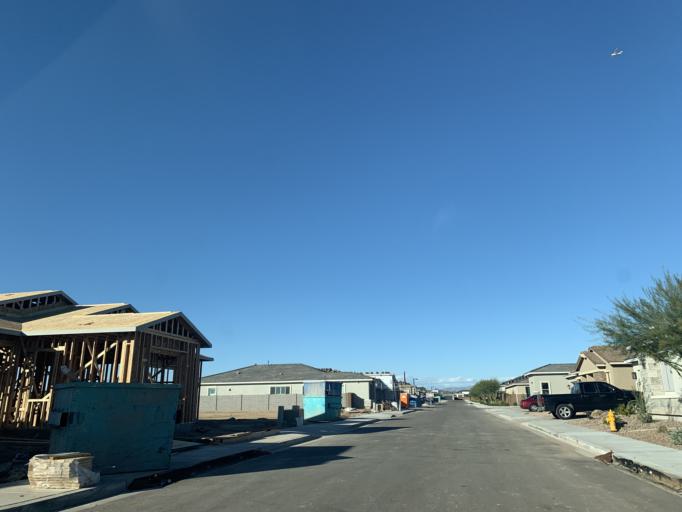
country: US
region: Arizona
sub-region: Maricopa County
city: Cave Creek
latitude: 33.6880
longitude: -112.0221
